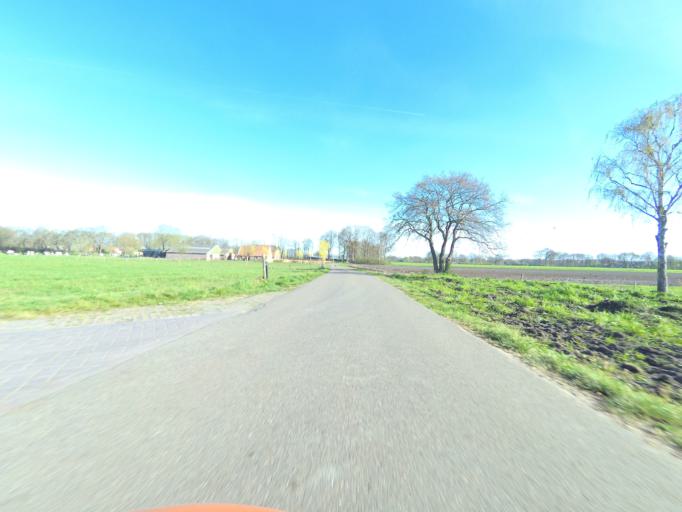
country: NL
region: Gelderland
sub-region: Gemeente Putten
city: Putten
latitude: 52.2354
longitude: 5.5916
